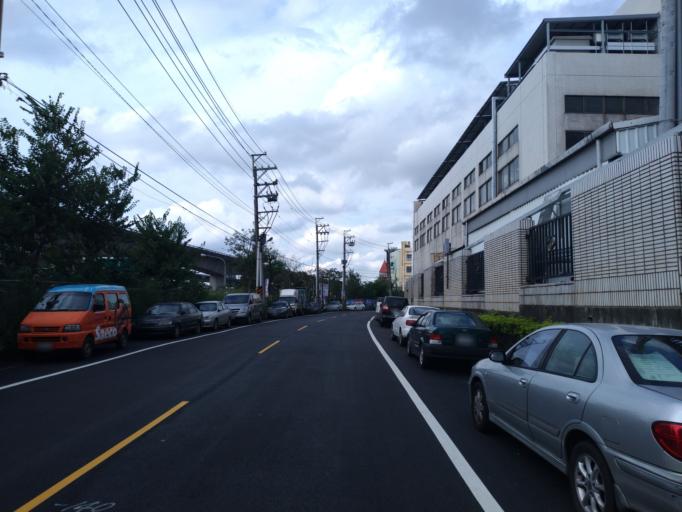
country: TW
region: Taiwan
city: Daxi
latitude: 24.9230
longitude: 121.1706
